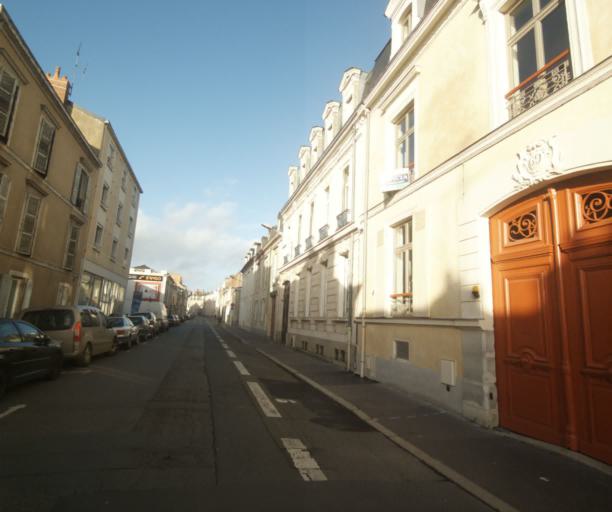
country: FR
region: Pays de la Loire
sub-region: Departement de la Sarthe
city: Le Mans
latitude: 47.9985
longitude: 0.2030
